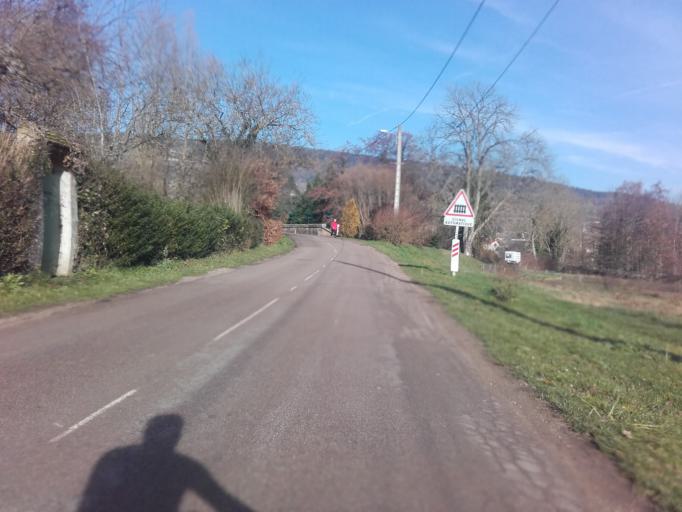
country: FR
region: Bourgogne
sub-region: Departement de Saone-et-Loire
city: Chagny
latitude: 46.9061
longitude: 4.6956
